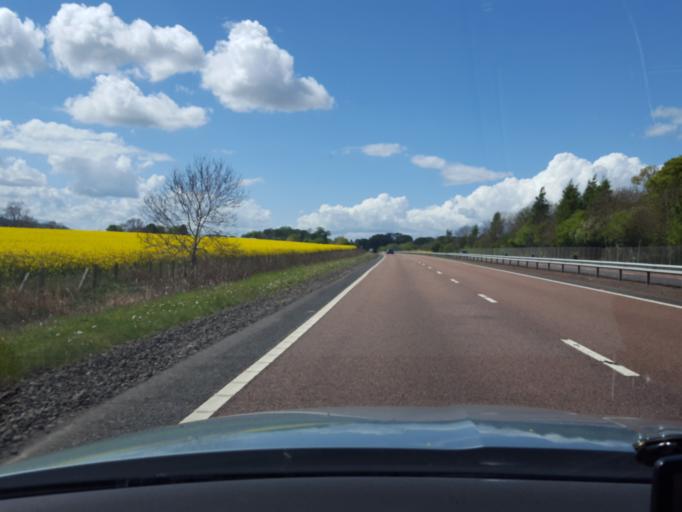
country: GB
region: Scotland
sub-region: Angus
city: Letham
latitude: 56.7175
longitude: -2.7753
